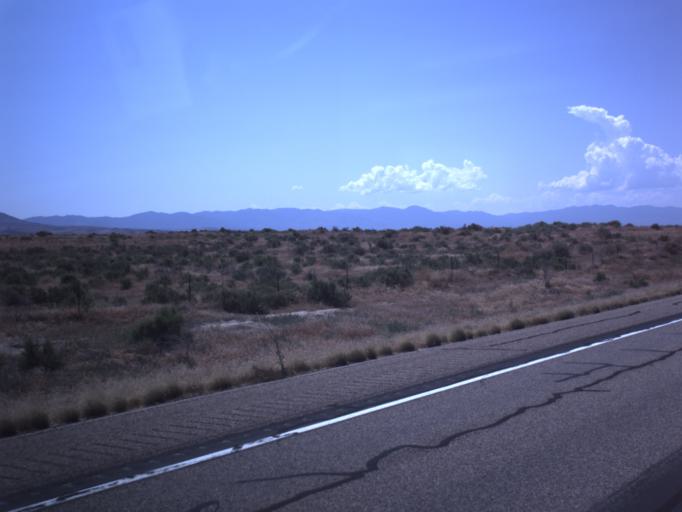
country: US
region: Utah
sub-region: Millard County
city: Delta
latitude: 39.3667
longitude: -112.4965
